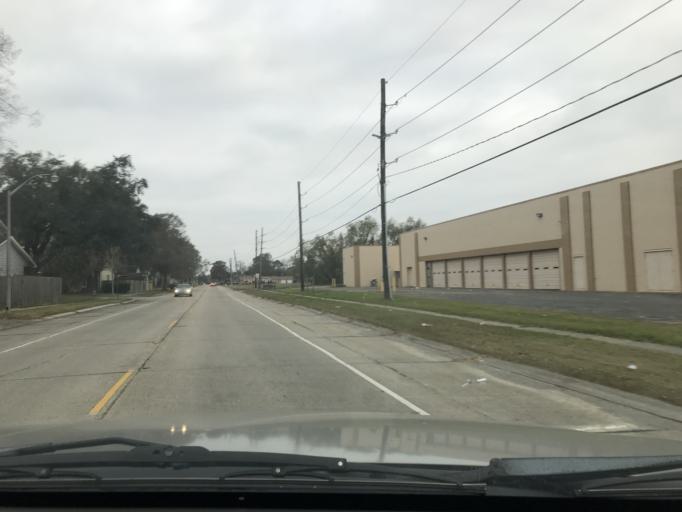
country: US
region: Louisiana
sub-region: Jefferson Parish
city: Woodmere
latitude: 29.8680
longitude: -90.0783
